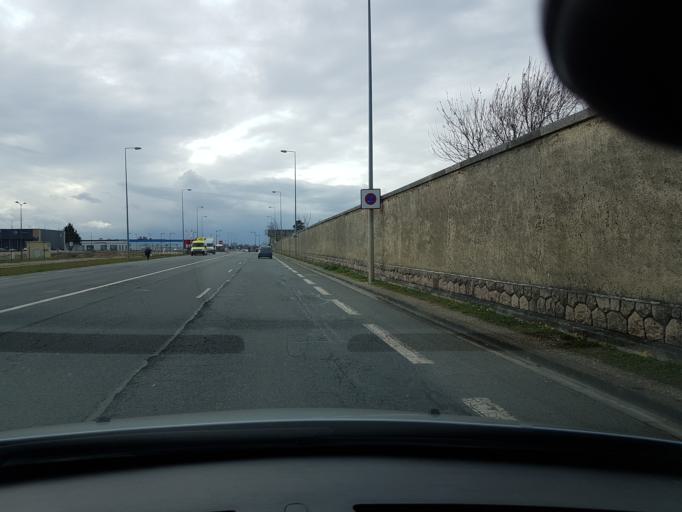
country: FR
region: Centre
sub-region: Departement du Cher
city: Bourges
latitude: 47.0961
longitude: 2.4391
